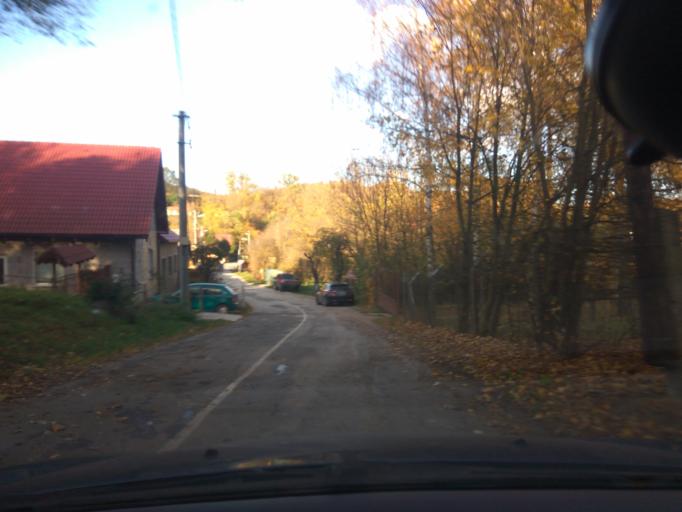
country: SK
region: Trnavsky
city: Vrbove
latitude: 48.6396
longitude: 17.6474
